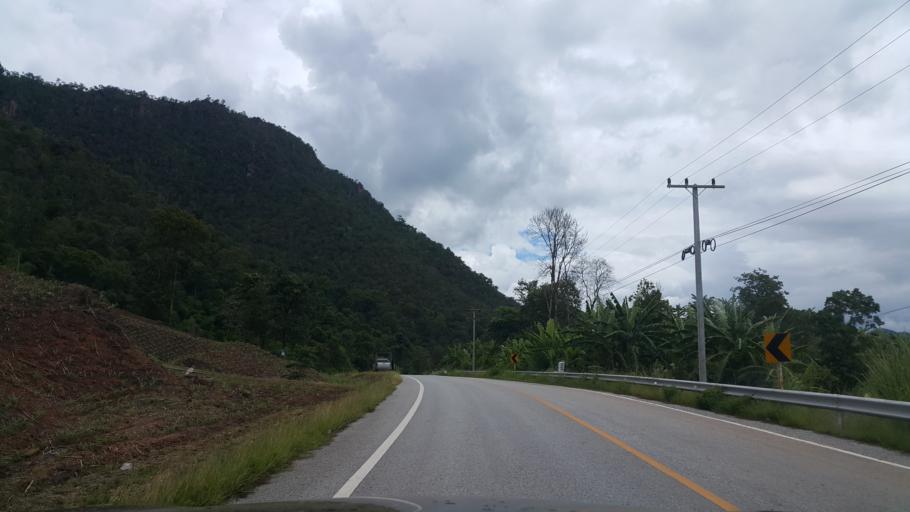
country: TH
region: Phitsanulok
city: Chat Trakan
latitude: 17.3661
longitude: 100.7389
